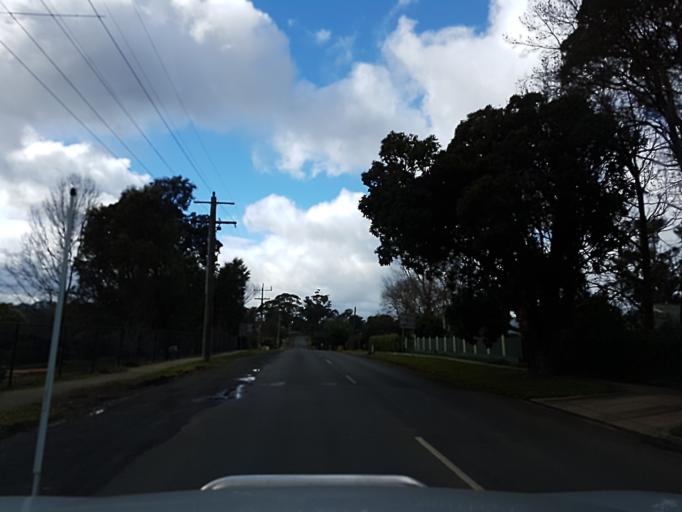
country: AU
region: Victoria
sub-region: Yarra Ranges
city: Monbulk
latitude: -37.8768
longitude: 145.4122
